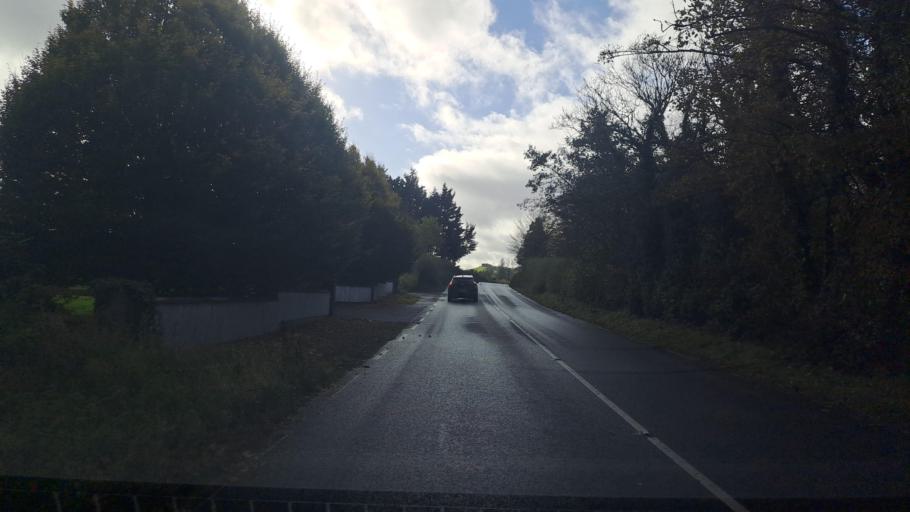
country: IE
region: Ulster
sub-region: County Monaghan
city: Monaghan
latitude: 54.2245
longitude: -6.9729
